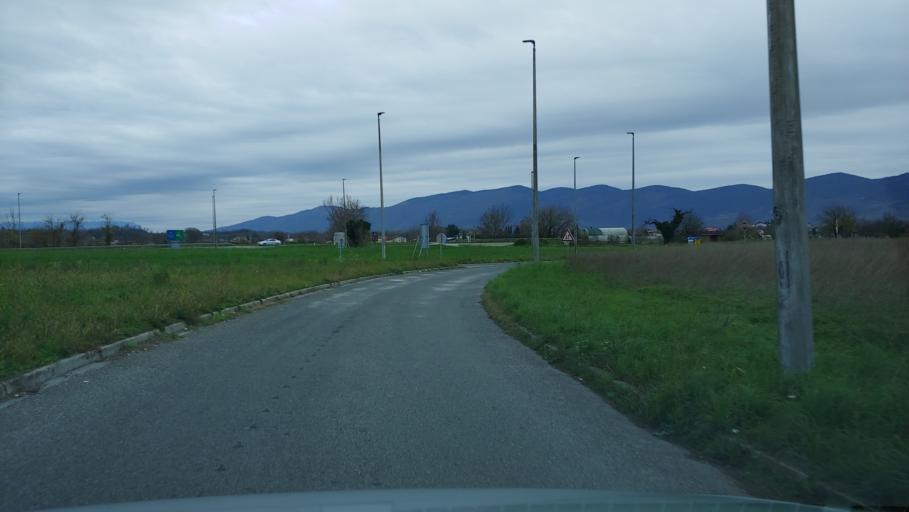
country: SI
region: Sempeter-Vrtojba
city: Vrtojba
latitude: 45.9186
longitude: 13.6278
